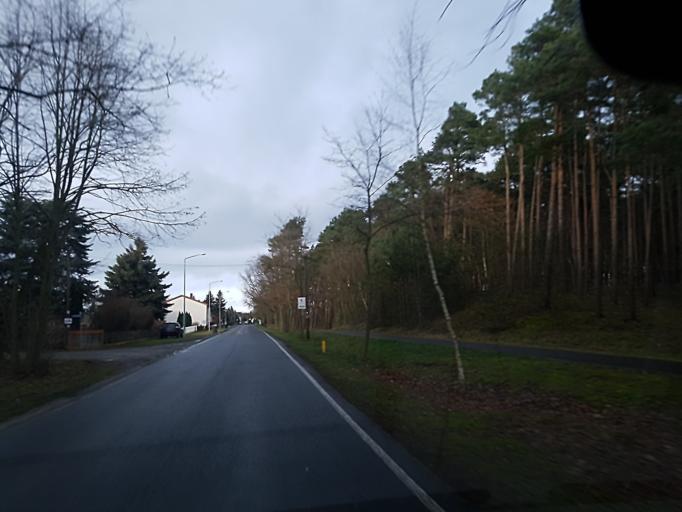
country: DE
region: Brandenburg
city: Elsterwerda
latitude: 51.4886
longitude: 13.5066
